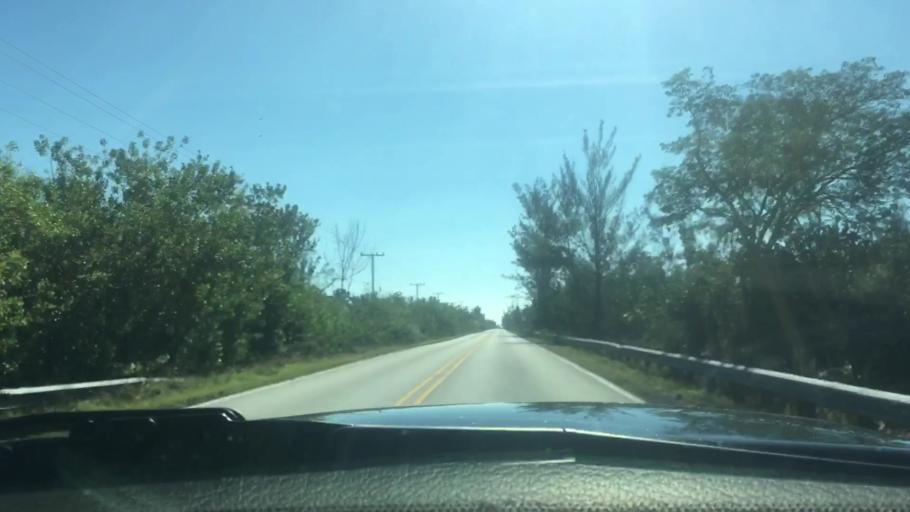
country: US
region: Florida
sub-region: Miami-Dade County
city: Florida City
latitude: 25.3725
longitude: -80.4335
